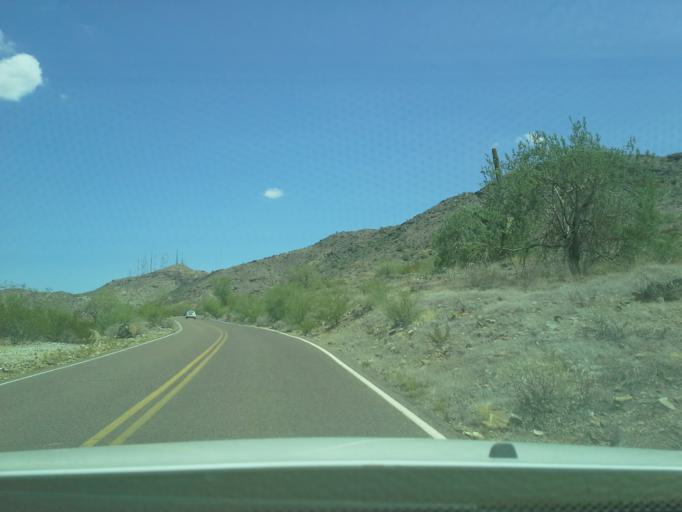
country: US
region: Arizona
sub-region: Maricopa County
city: Laveen
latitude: 33.3323
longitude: -112.0944
